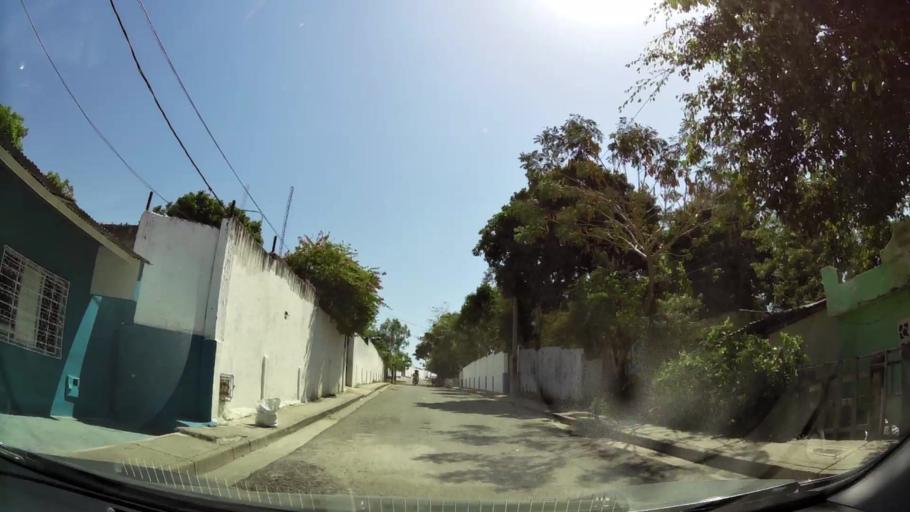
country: CO
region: Bolivar
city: Cartagena
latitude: 10.4269
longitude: -75.5263
